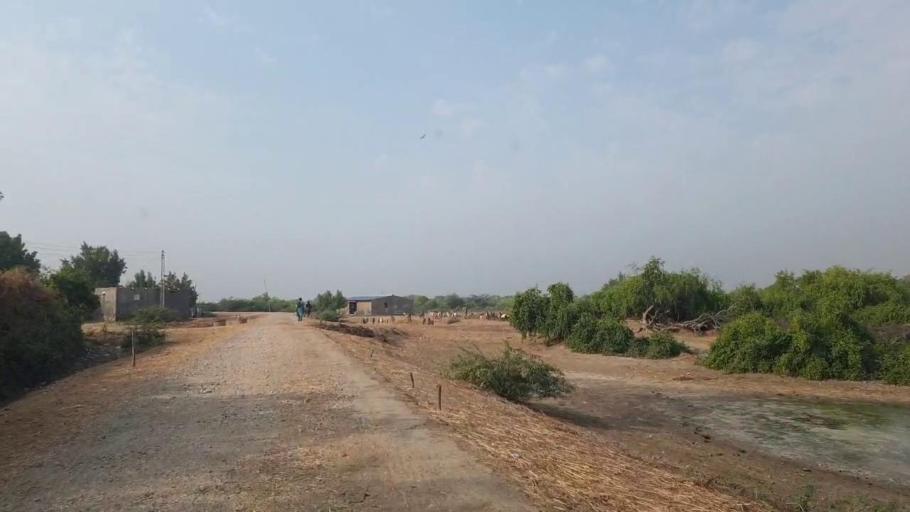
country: PK
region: Sindh
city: Tando Bago
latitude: 24.7733
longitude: 68.8684
